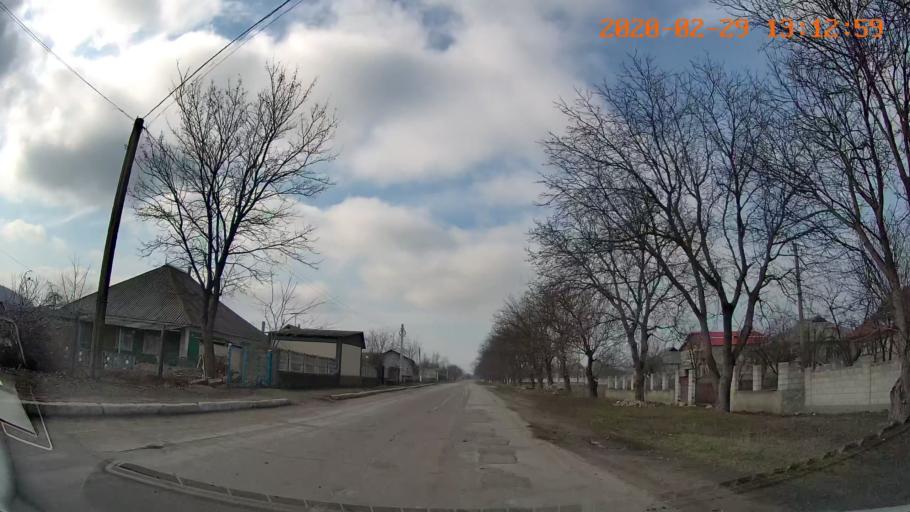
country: MD
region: Telenesti
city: Camenca
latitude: 48.0136
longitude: 28.6896
